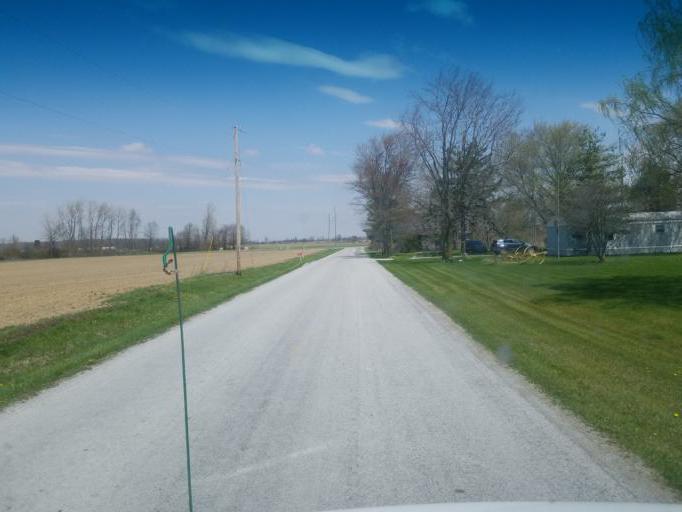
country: US
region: Ohio
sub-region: Hardin County
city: Forest
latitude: 40.7580
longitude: -83.5378
